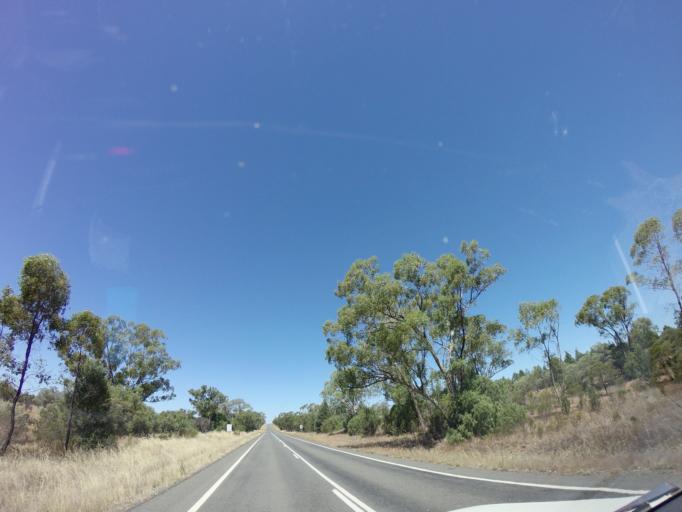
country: AU
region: New South Wales
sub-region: Bogan
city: Nyngan
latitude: -31.5500
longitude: 146.6850
